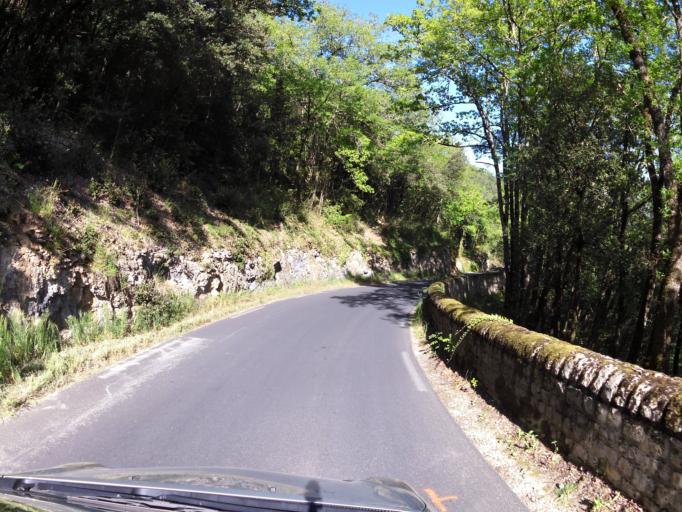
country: FR
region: Aquitaine
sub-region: Departement de la Dordogne
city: Carsac-Aillac
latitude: 44.8437
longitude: 1.2633
